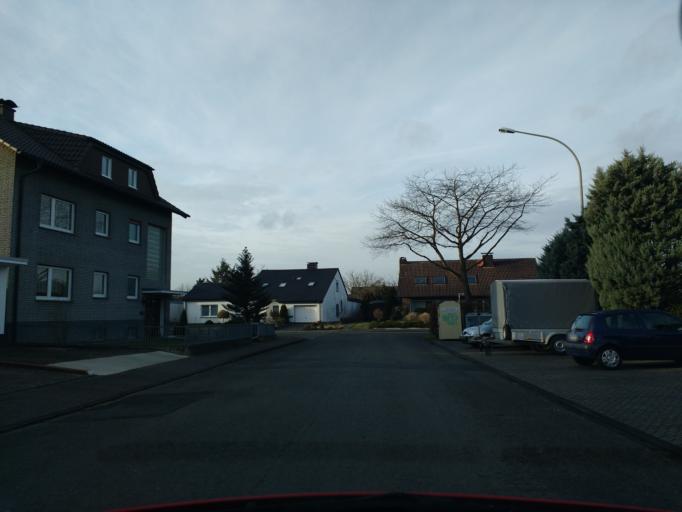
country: DE
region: North Rhine-Westphalia
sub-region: Regierungsbezirk Detmold
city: Paderborn
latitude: 51.7628
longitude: 8.7285
